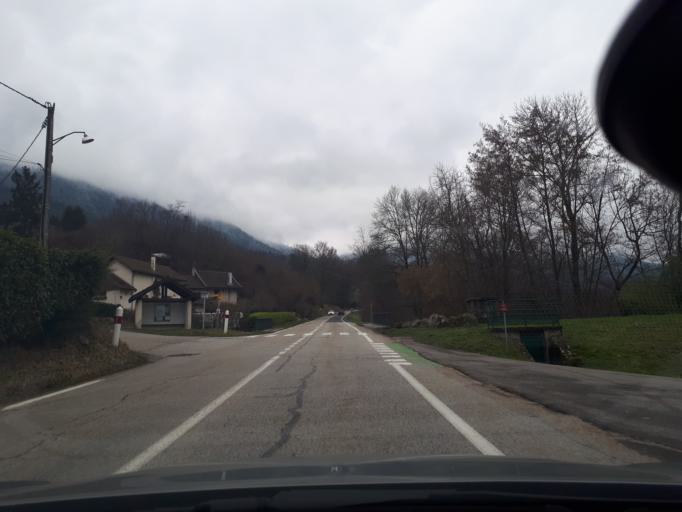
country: FR
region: Rhone-Alpes
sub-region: Departement de l'Isere
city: Vaulnaveys-le-Haut
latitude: 45.1293
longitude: 5.8262
